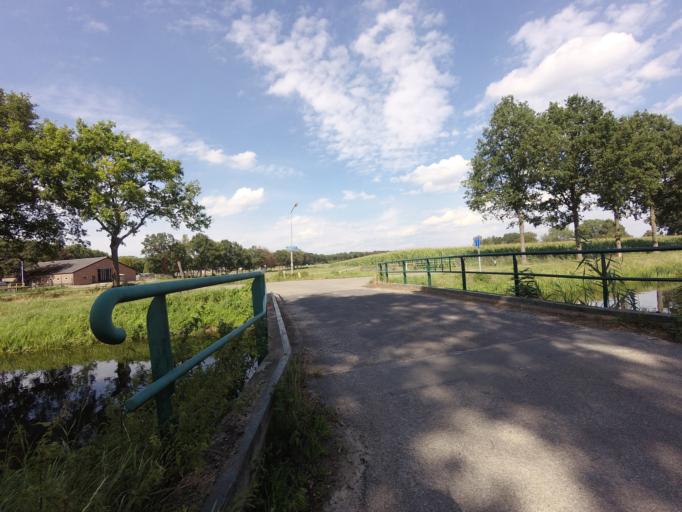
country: NL
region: Overijssel
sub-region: Gemeente Deventer
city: Schalkhaar
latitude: 52.2794
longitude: 6.2429
